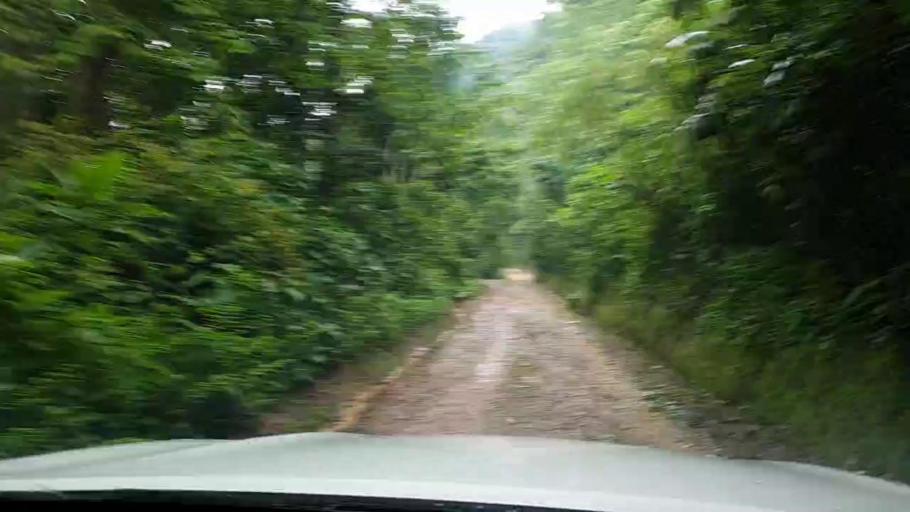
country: RW
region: Western Province
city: Cyangugu
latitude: -2.5587
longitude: 28.9841
